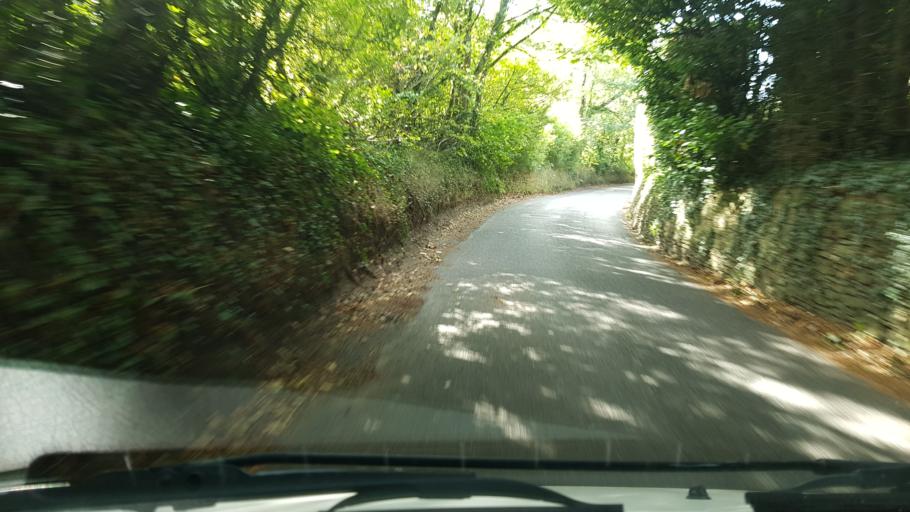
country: GB
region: England
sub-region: Surrey
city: Godalming
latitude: 51.2220
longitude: -0.6296
